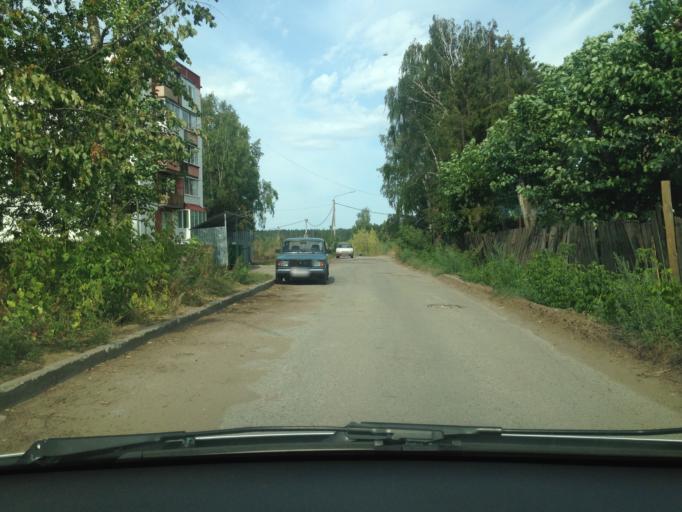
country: RU
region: Udmurtiya
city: Izhevsk
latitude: 56.8752
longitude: 53.1968
